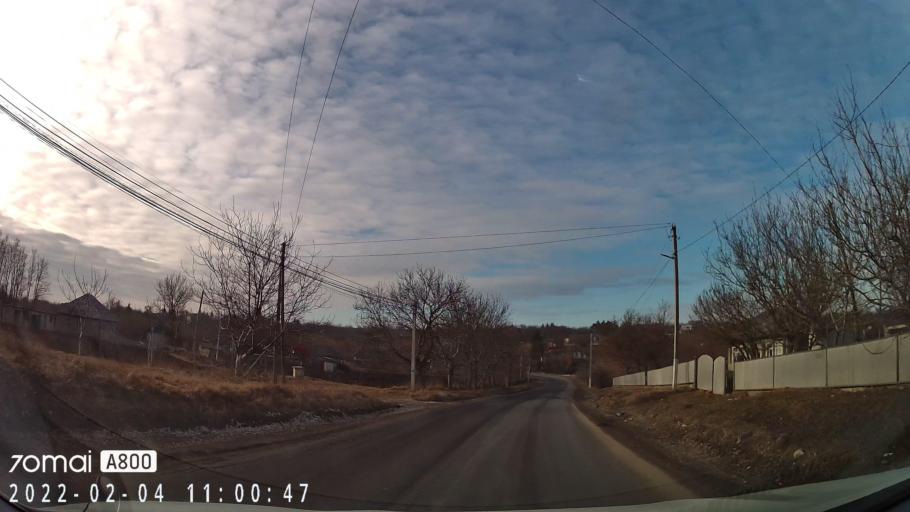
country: RO
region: Botosani
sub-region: Comuna Radauti-Prut
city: Miorcani
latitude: 48.2976
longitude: 26.9396
